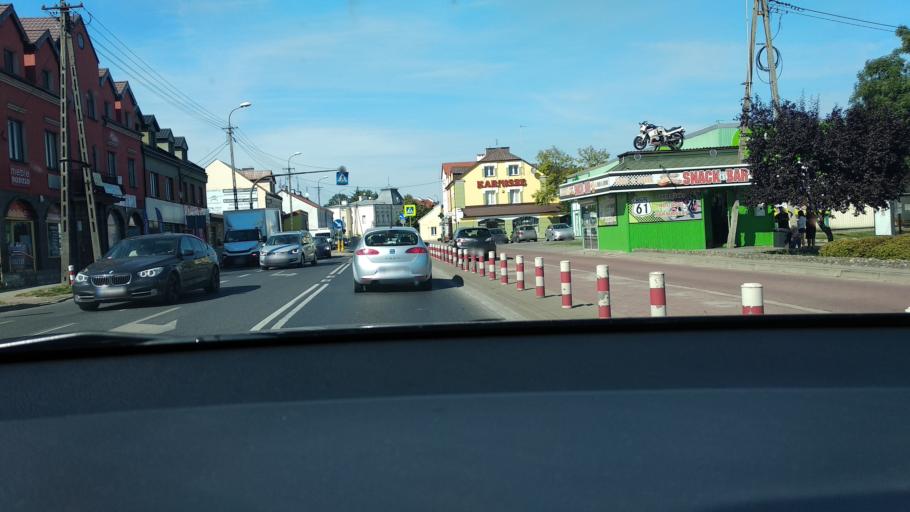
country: PL
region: Masovian Voivodeship
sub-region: Powiat pultuski
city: Pultusk
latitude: 52.7012
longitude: 21.0855
